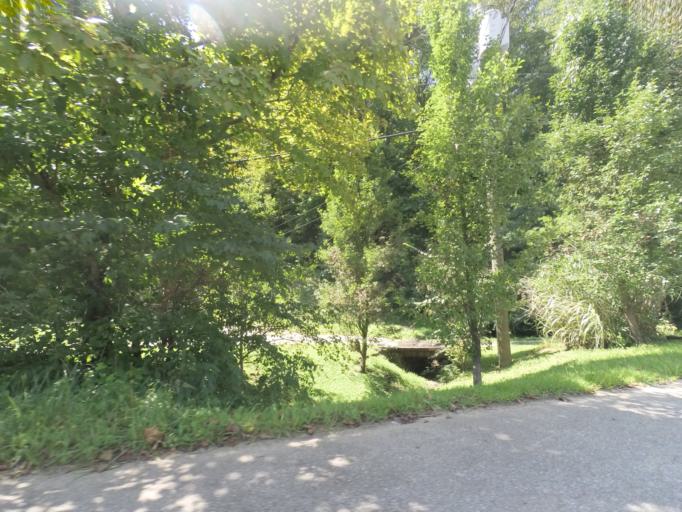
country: US
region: West Virginia
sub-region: Cabell County
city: Huntington
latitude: 38.3894
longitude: -82.4523
